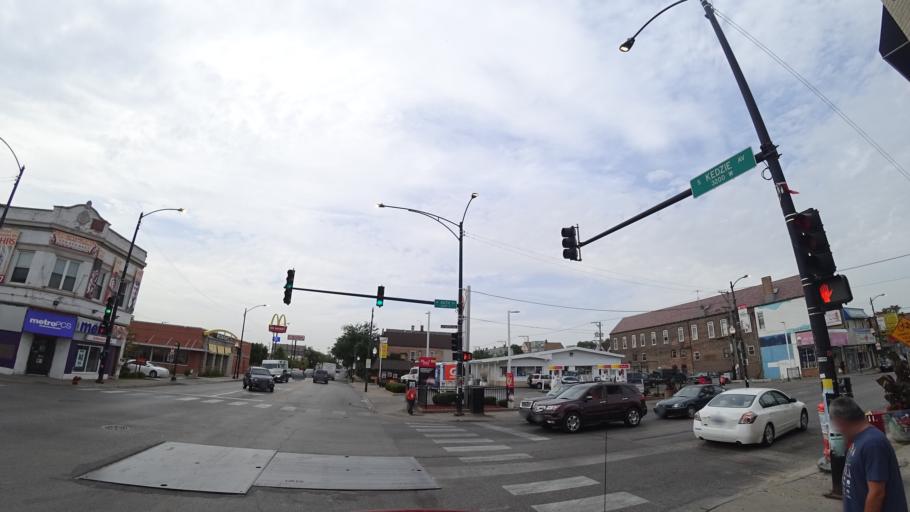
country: US
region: Illinois
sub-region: Cook County
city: Cicero
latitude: 41.8448
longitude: -87.7051
